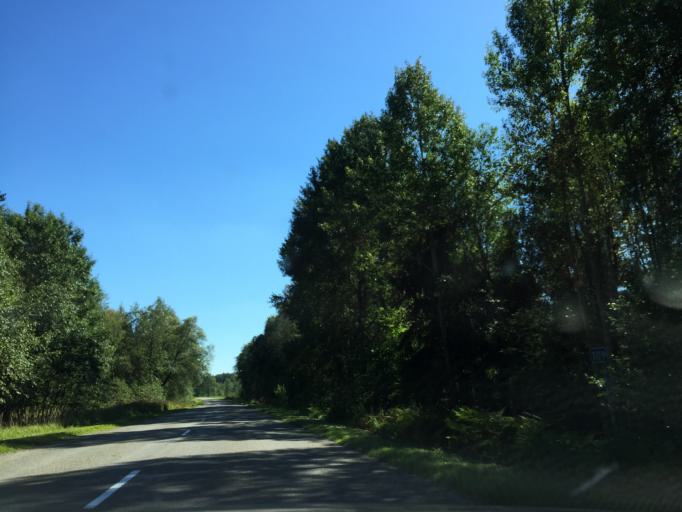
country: LV
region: Akniste
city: Akniste
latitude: 56.0815
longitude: 25.8782
